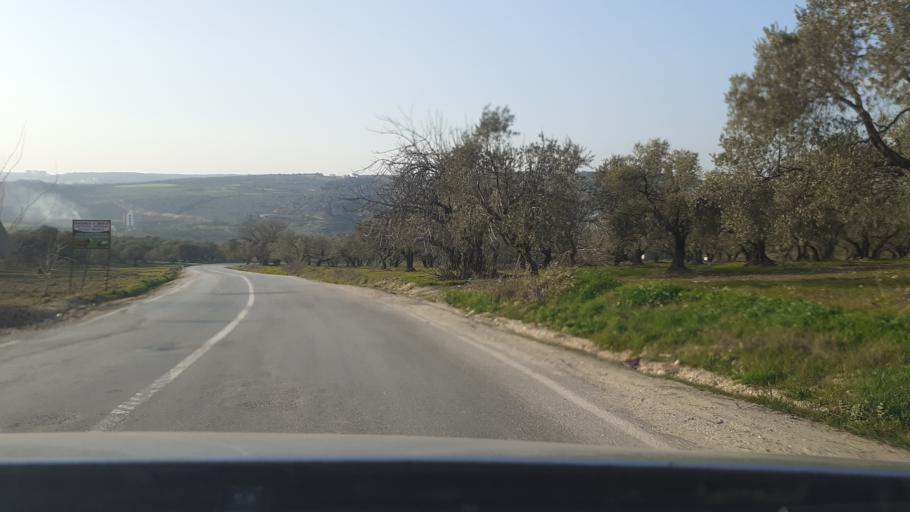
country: TR
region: Hatay
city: Oymakli
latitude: 36.1138
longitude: 36.2859
